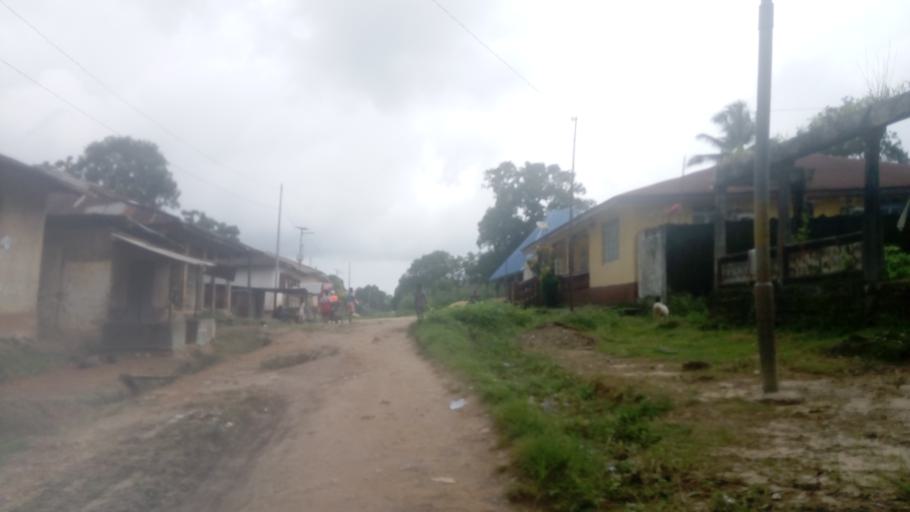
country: SL
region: Northern Province
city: Lunsar
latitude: 8.6817
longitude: -12.5365
